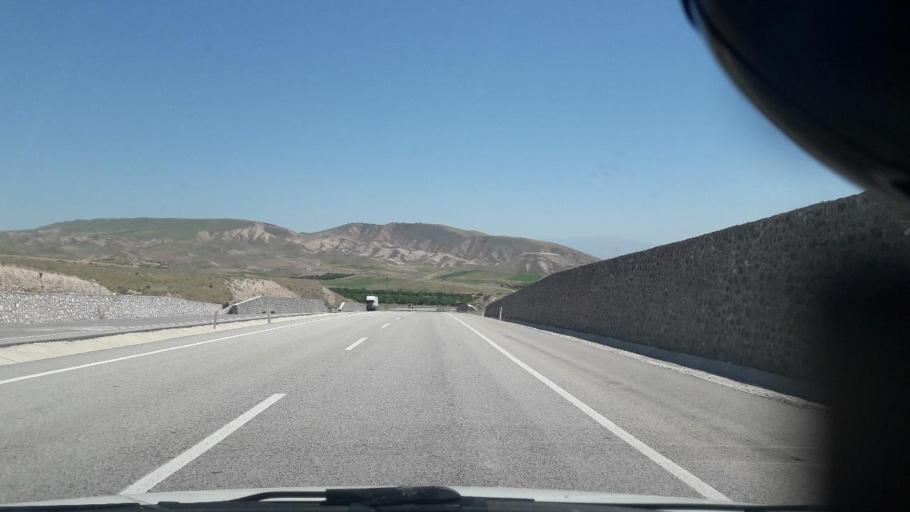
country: TR
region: Malatya
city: Yazihan
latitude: 38.6636
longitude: 38.1538
